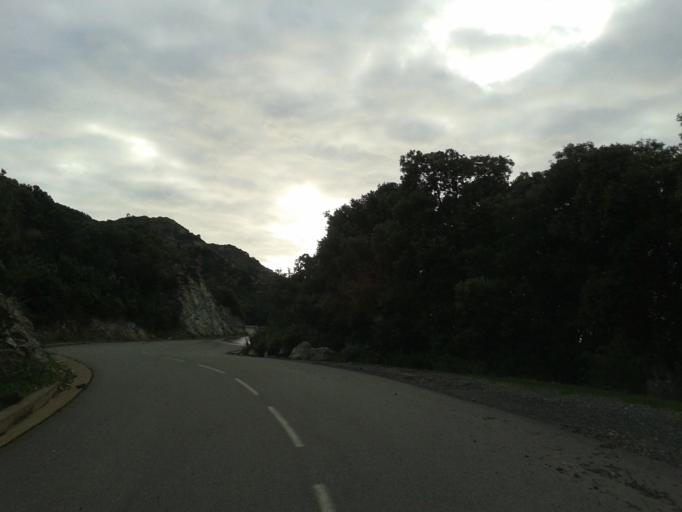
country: FR
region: Corsica
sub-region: Departement de la Haute-Corse
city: Brando
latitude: 42.8648
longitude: 9.3442
